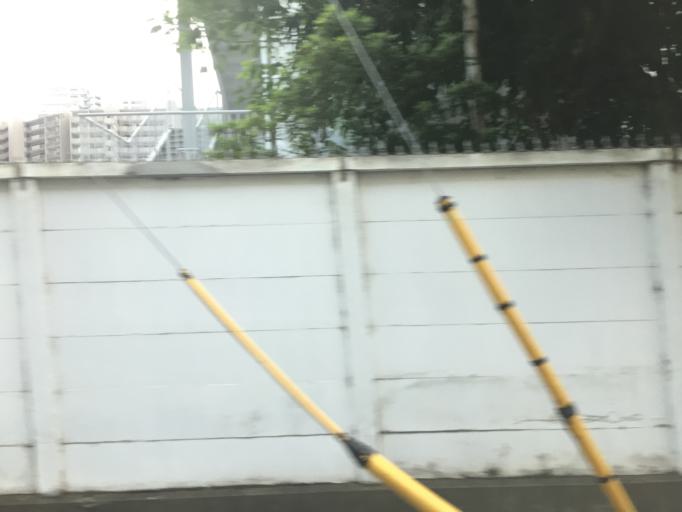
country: JP
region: Kanagawa
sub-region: Kawasaki-shi
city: Kawasaki
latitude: 35.5663
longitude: 139.6844
